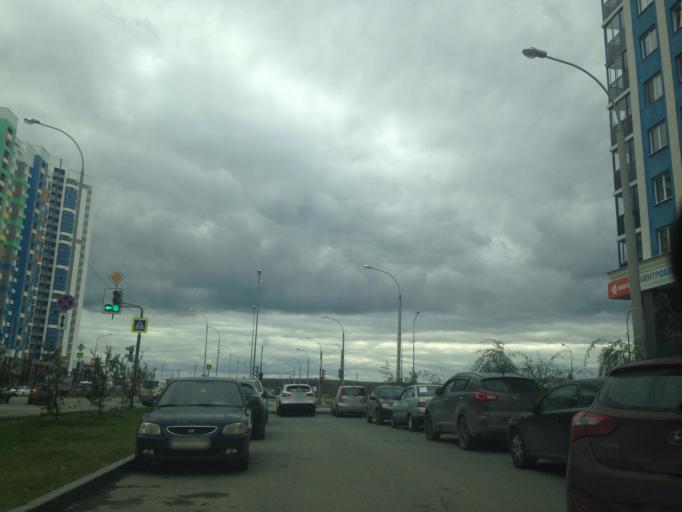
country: RU
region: Sverdlovsk
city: Shirokaya Rechka
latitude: 56.7901
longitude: 60.5154
